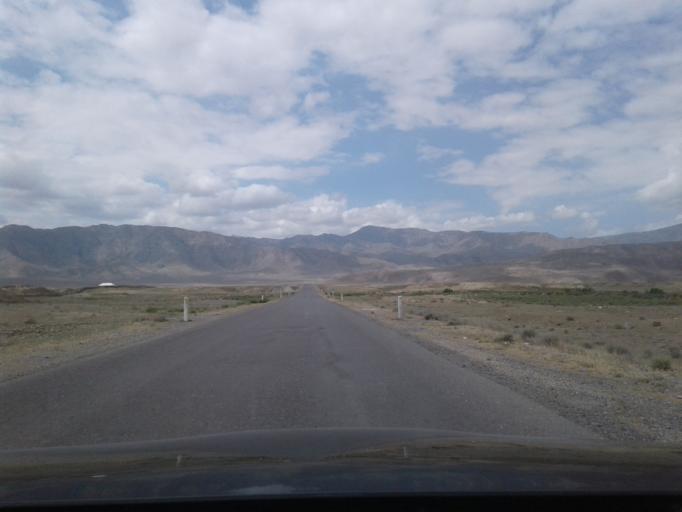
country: TM
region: Ahal
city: Baharly
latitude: 38.5319
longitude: 57.1502
